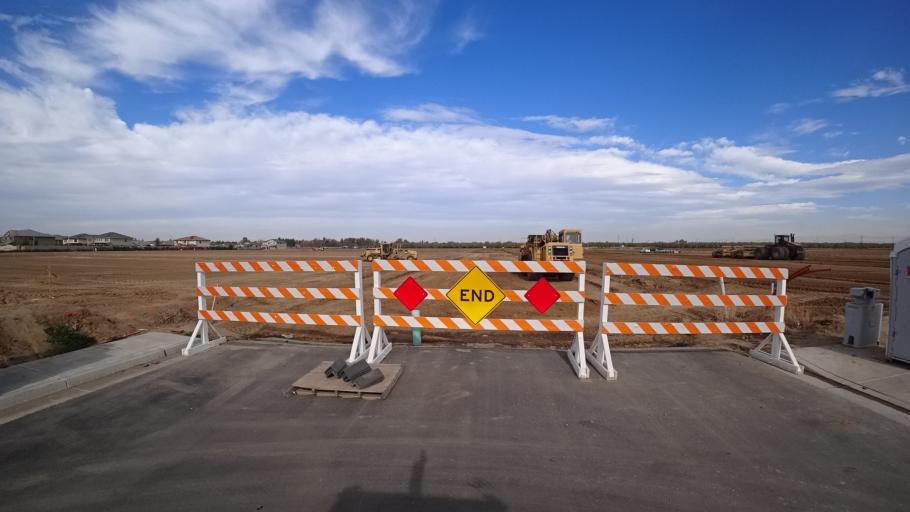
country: US
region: California
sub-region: Kern County
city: Greenacres
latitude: 35.4305
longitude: -119.0995
